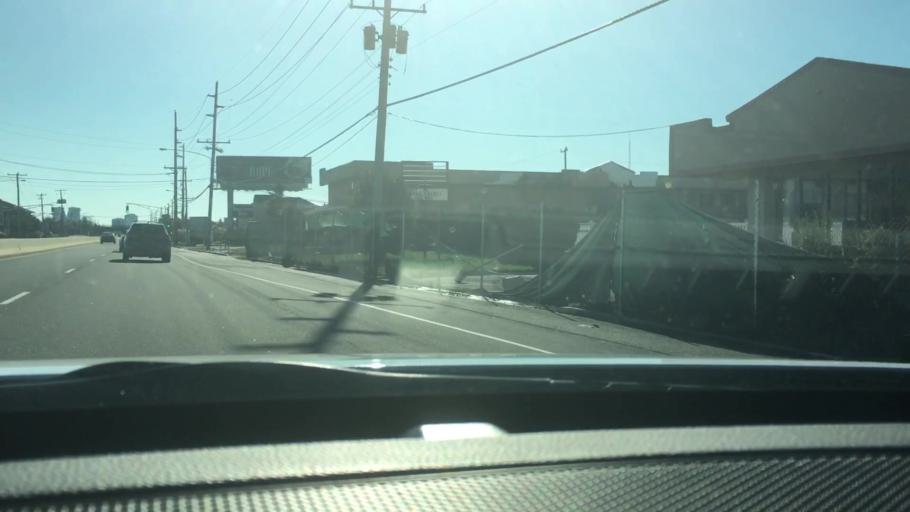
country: US
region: New Jersey
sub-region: Atlantic County
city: Ventnor City
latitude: 39.3720
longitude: -74.4791
